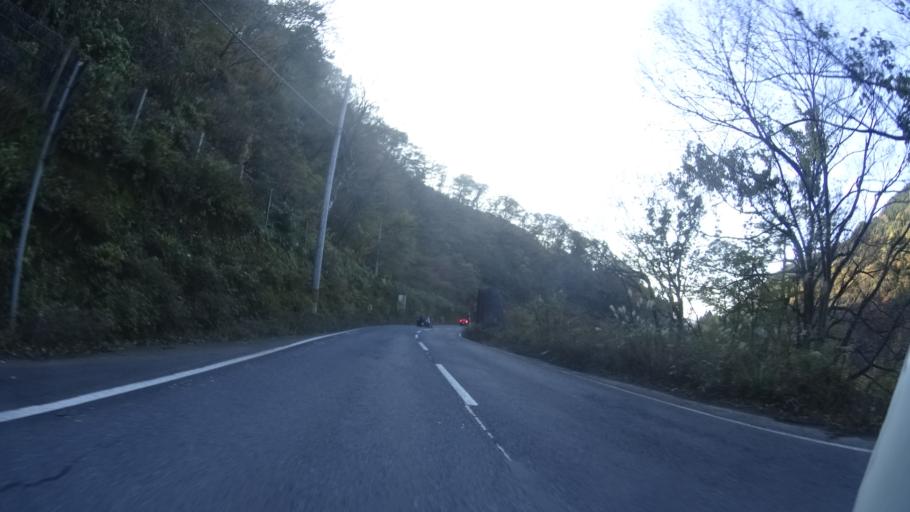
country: JP
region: Fukui
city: Ono
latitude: 35.9648
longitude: 136.5901
